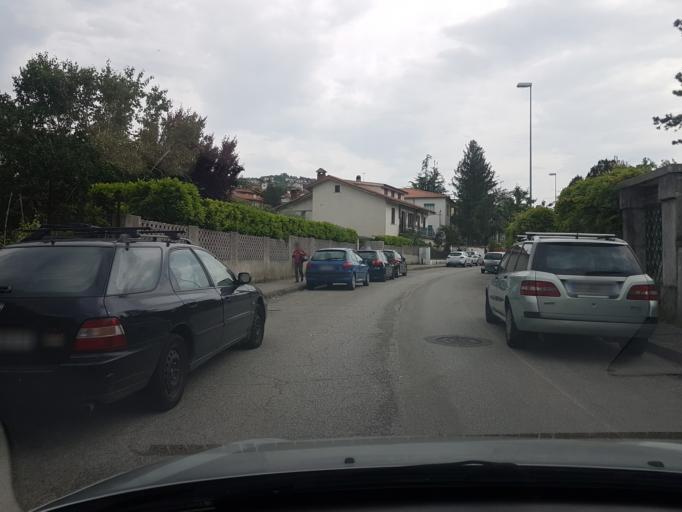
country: IT
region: Friuli Venezia Giulia
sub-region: Provincia di Trieste
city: Muggia
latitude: 45.6010
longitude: 13.7678
